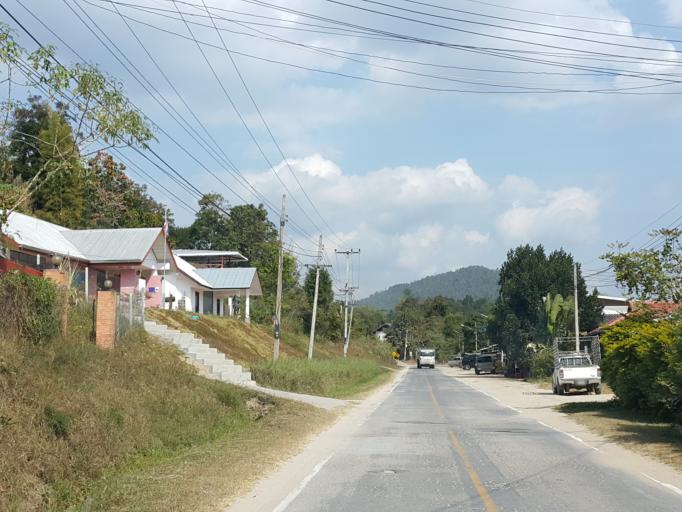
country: TH
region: Chiang Mai
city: Om Koi
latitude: 17.7990
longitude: 98.3622
